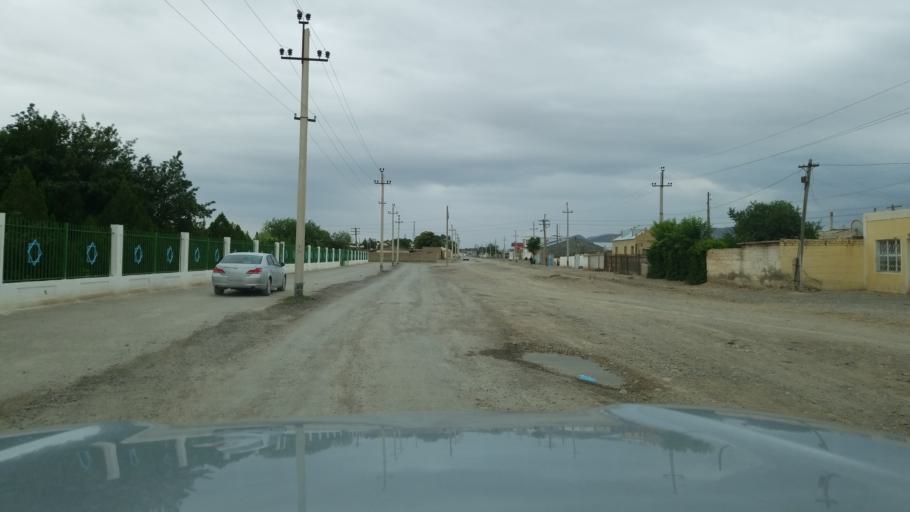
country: TM
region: Balkan
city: Serdar
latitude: 38.9848
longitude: 56.2588
